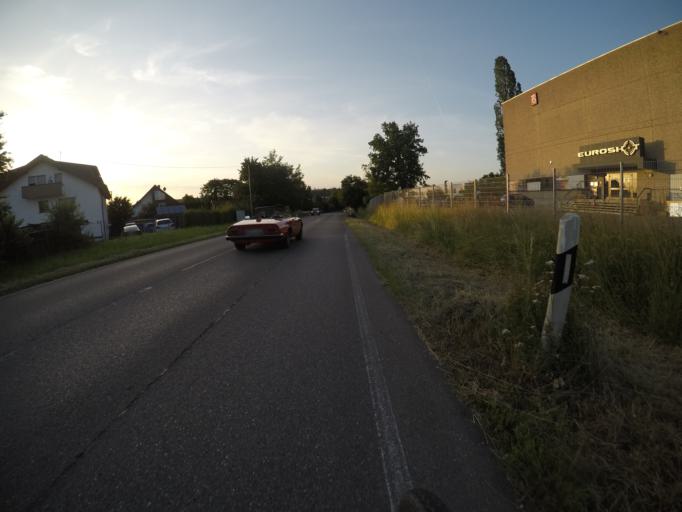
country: DE
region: Baden-Wuerttemberg
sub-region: Regierungsbezirk Stuttgart
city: Steinenbronn
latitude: 48.6643
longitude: 9.1238
